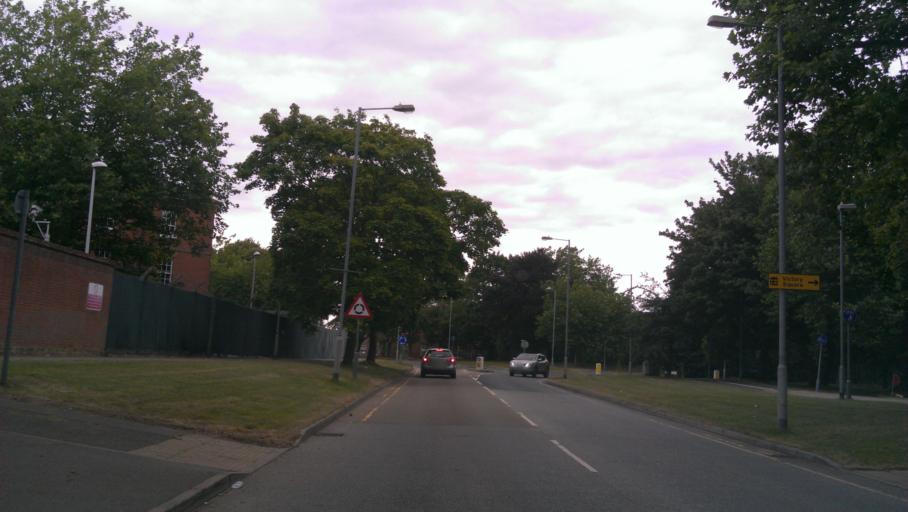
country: GB
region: England
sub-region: Essex
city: Colchester
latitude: 51.8795
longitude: 0.8910
